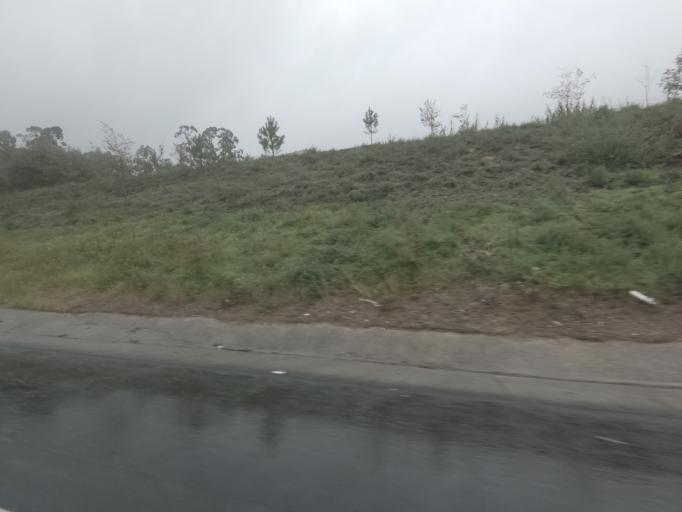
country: ES
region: Galicia
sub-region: Provincia de Pontevedra
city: Redondela
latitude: 42.2351
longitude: -8.6532
